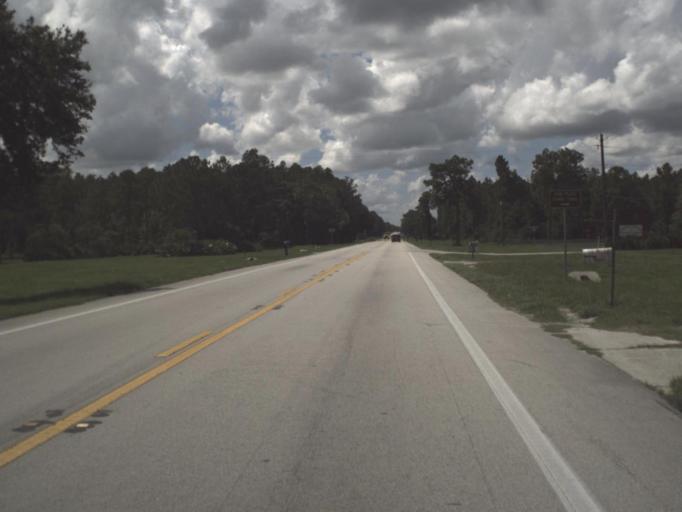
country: US
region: Florida
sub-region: Polk County
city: Polk City
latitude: 28.3274
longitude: -81.8338
